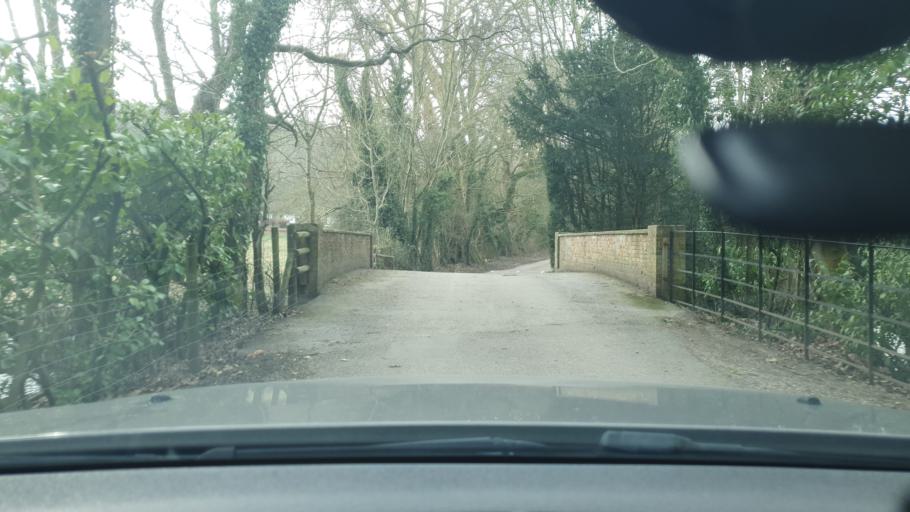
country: GB
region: England
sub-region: Wiltshire
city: Ramsbury
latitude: 51.4378
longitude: -1.6232
